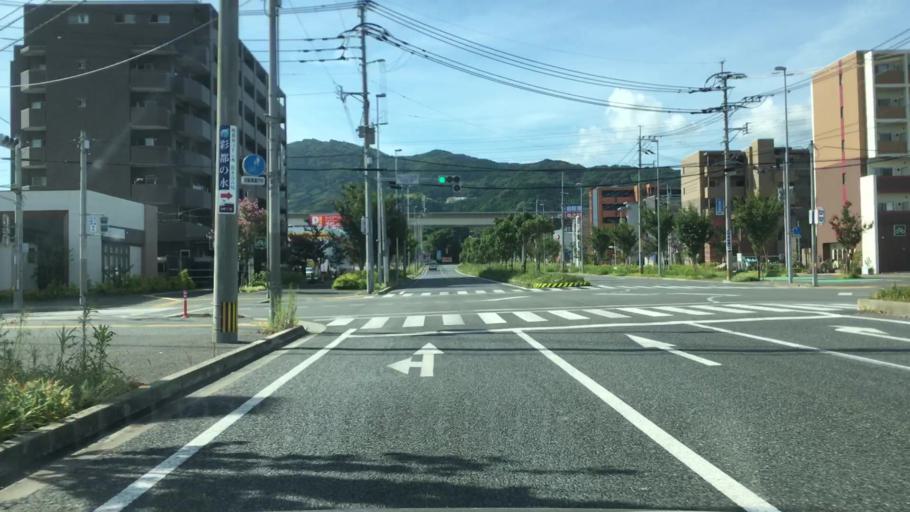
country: JP
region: Fukuoka
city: Maebaru-chuo
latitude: 33.5760
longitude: 130.2563
